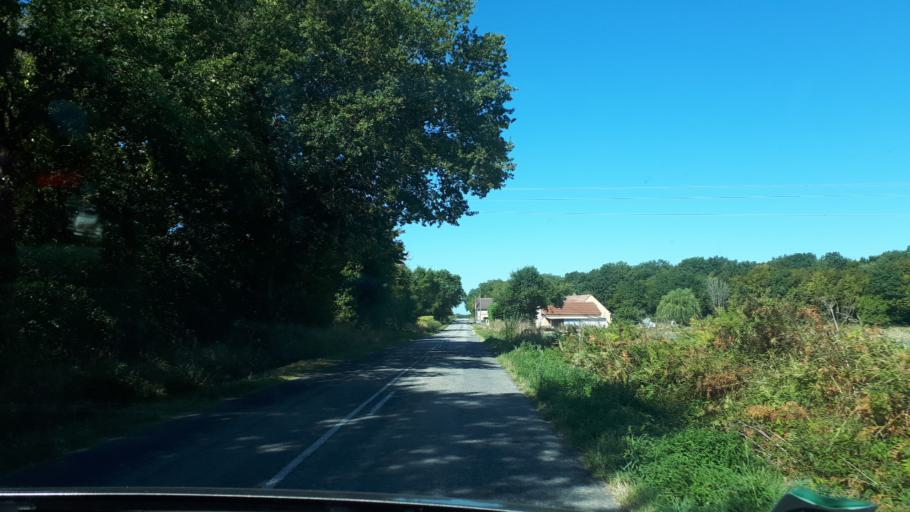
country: FR
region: Centre
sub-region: Departement du Loiret
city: Autry-le-Chatel
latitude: 47.5948
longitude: 2.6216
